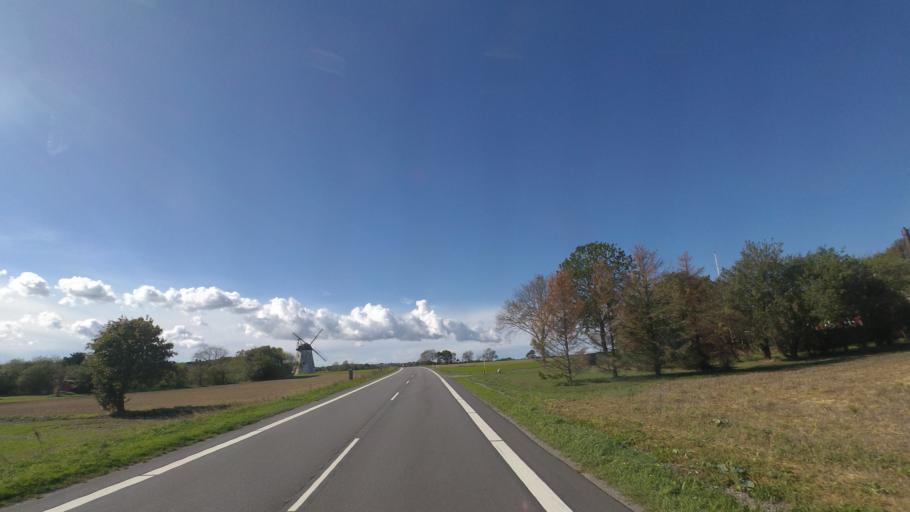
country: DK
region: Capital Region
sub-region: Bornholm Kommune
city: Akirkeby
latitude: 55.0692
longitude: 14.9683
